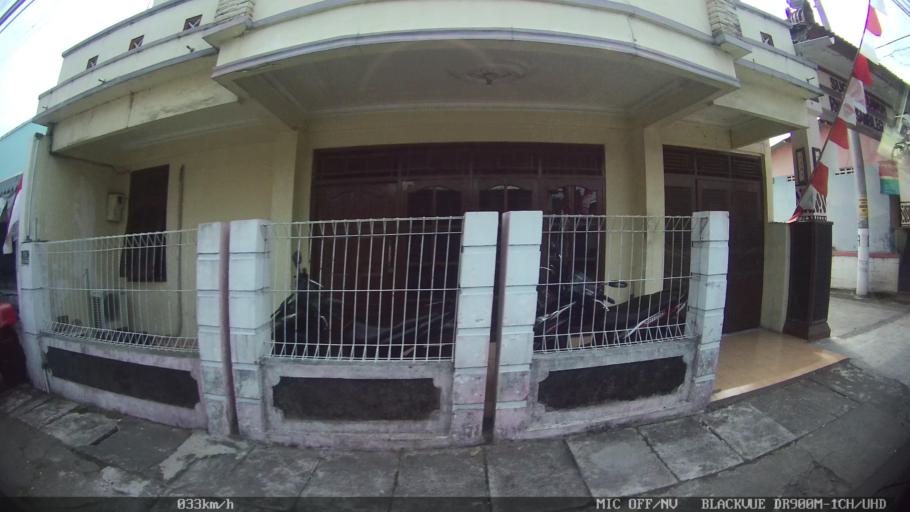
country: ID
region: Daerah Istimewa Yogyakarta
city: Depok
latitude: -7.7777
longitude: 110.4351
